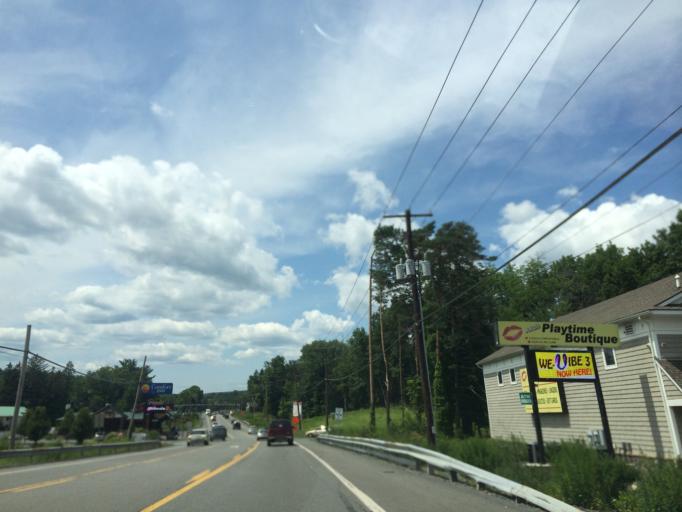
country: US
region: Pennsylvania
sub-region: Monroe County
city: Tannersville
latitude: 41.0034
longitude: -75.2755
